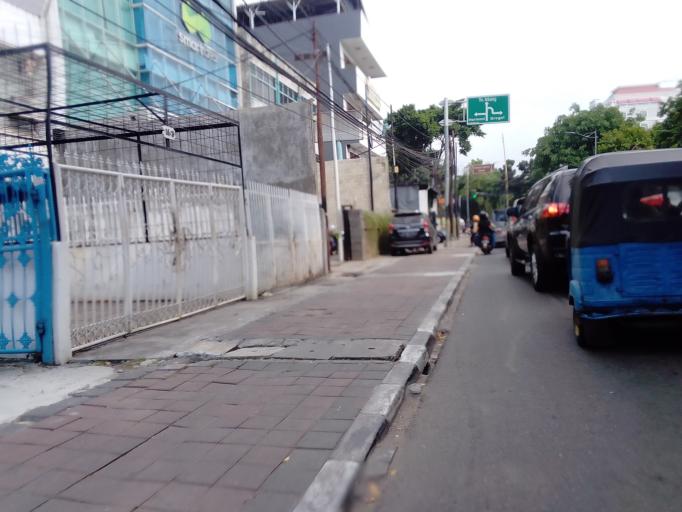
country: ID
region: Jakarta Raya
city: Jakarta
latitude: -6.1649
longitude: 106.8107
